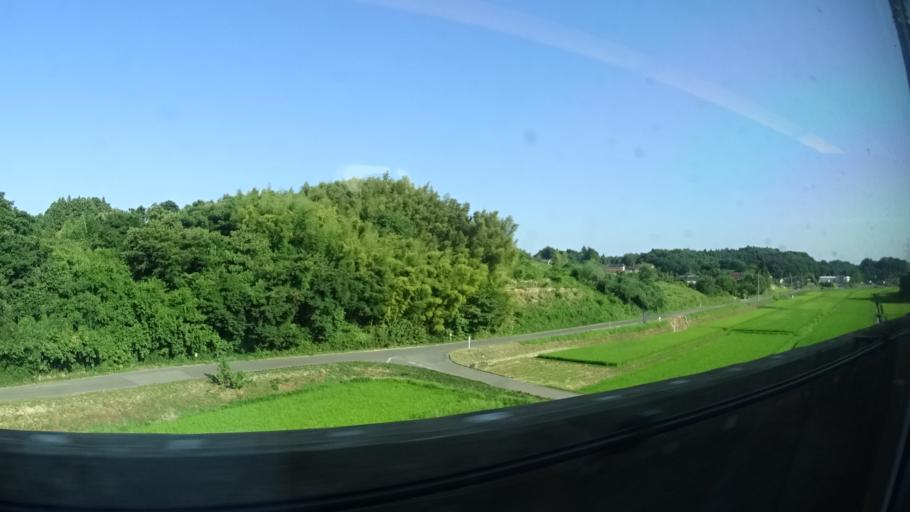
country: JP
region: Fukushima
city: Motomiya
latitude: 37.5181
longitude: 140.4331
